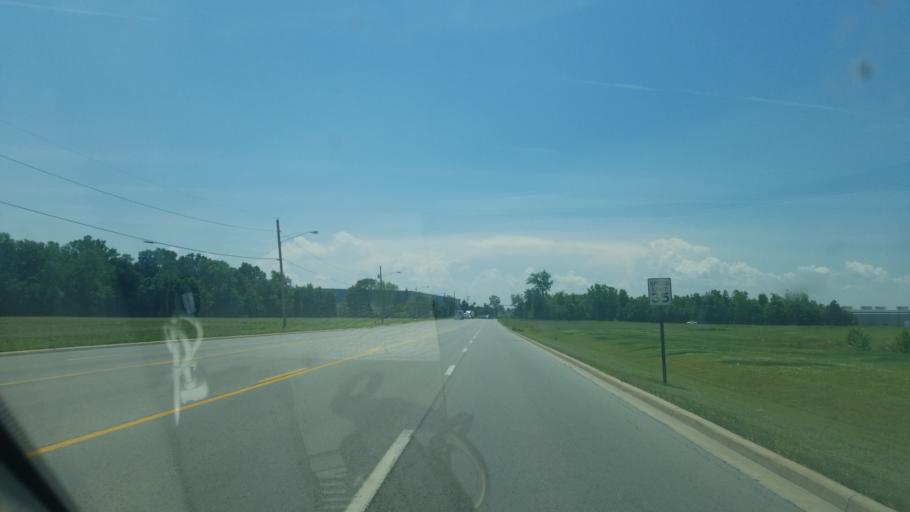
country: US
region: Ohio
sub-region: Hancock County
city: Findlay
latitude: 41.0761
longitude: -83.6176
